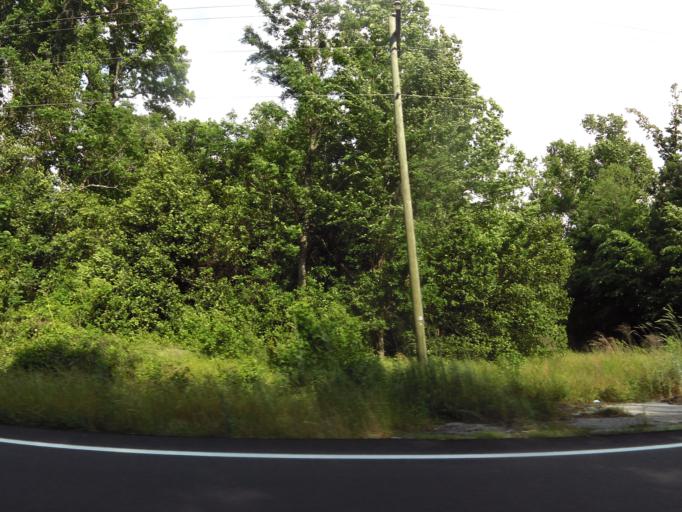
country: US
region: South Carolina
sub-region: Allendale County
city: Fairfax
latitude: 32.9793
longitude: -81.2284
